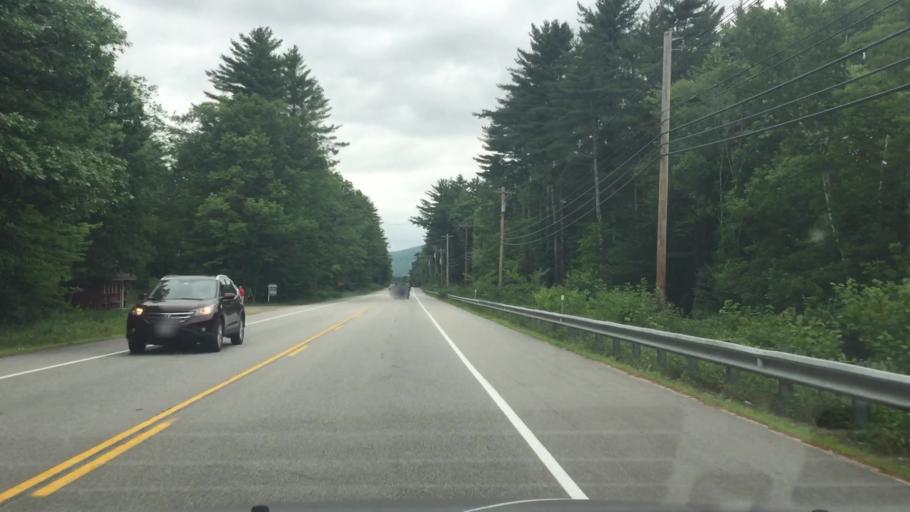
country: US
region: New Hampshire
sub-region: Carroll County
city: Center Harbor
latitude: 43.6905
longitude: -71.4585
